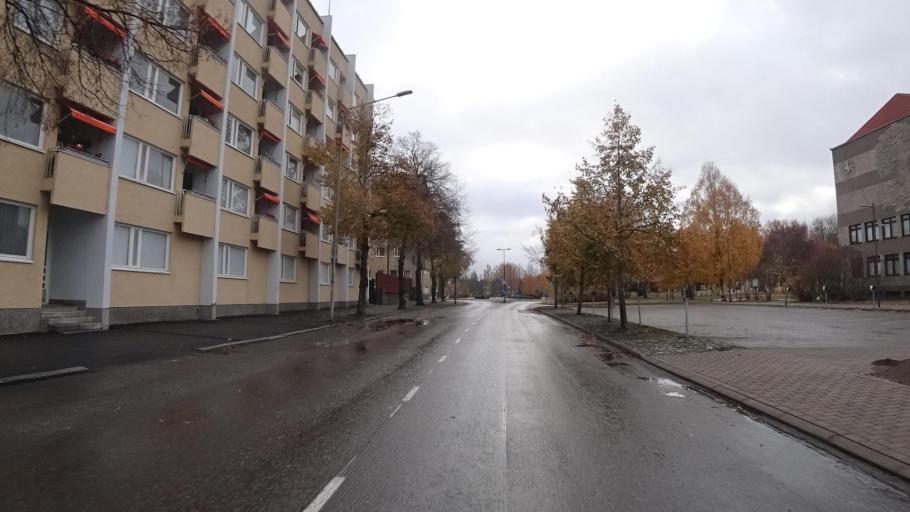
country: FI
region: Northern Savo
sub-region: Varkaus
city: Varkaus
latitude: 62.3131
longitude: 27.8870
